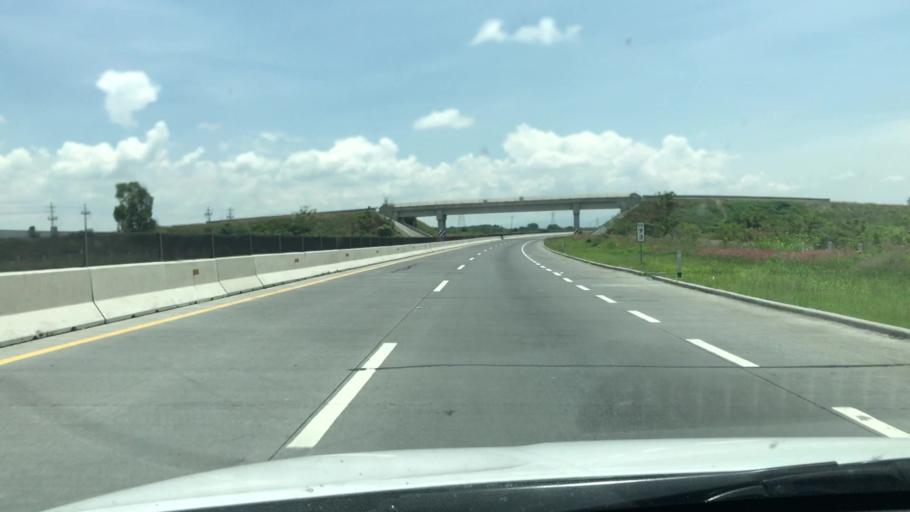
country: MX
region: Michoacan
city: La Piedad Cavadas
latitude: 20.3894
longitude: -102.1061
